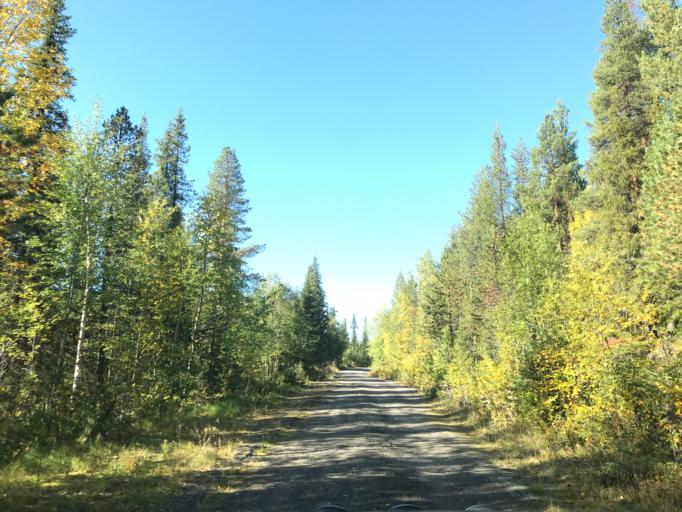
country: SE
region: Norrbotten
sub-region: Gallivare Kommun
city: Malmberget
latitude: 67.6457
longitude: 21.1095
